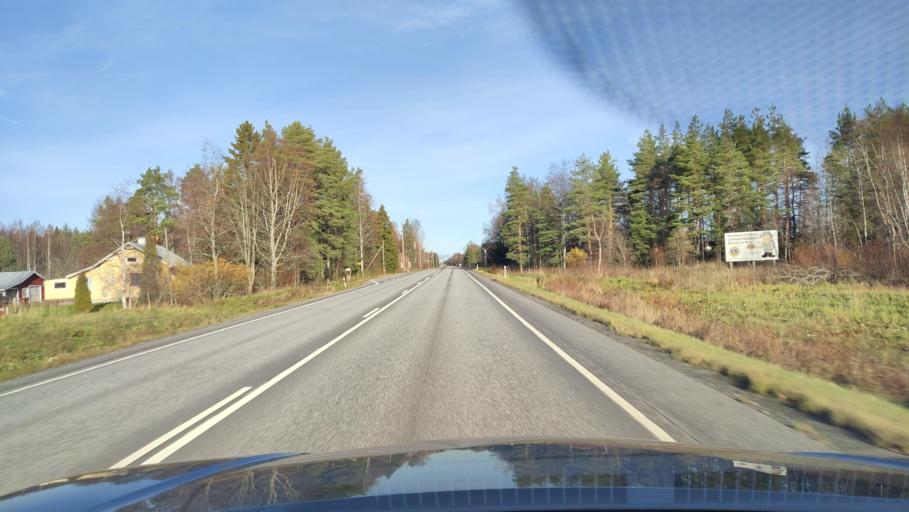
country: FI
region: Ostrobothnia
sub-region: Vaasa
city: Malax
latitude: 62.7705
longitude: 21.6575
